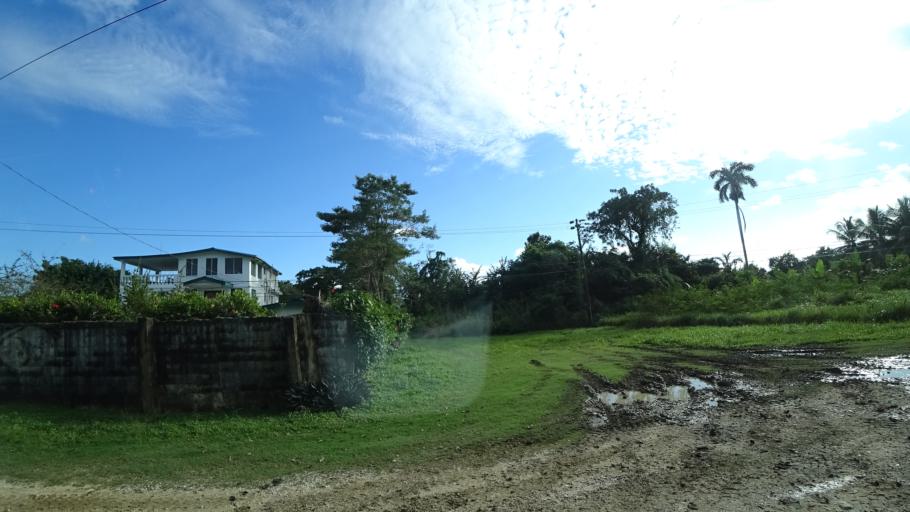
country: BZ
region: Belize
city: Belize City
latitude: 17.5700
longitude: -88.3972
